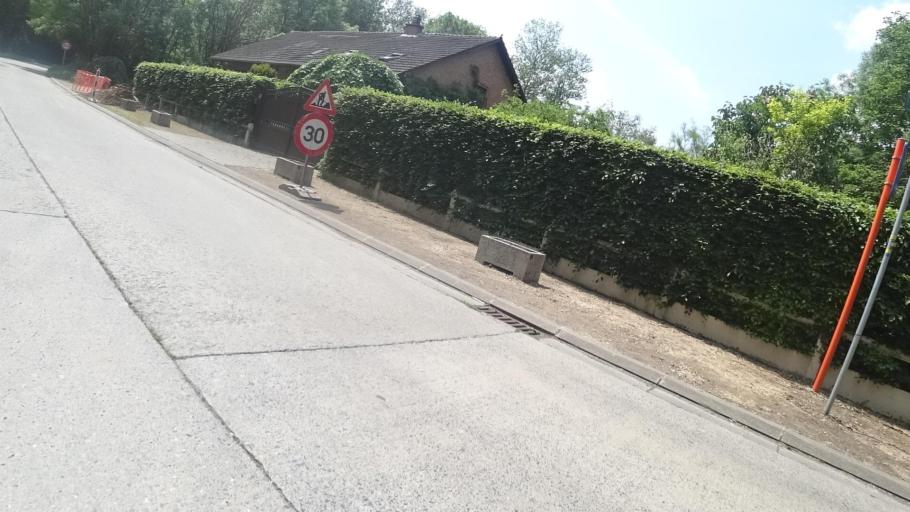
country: BE
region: Wallonia
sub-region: Province du Brabant Wallon
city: Louvain-la-Neuve
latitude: 50.6938
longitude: 4.6388
